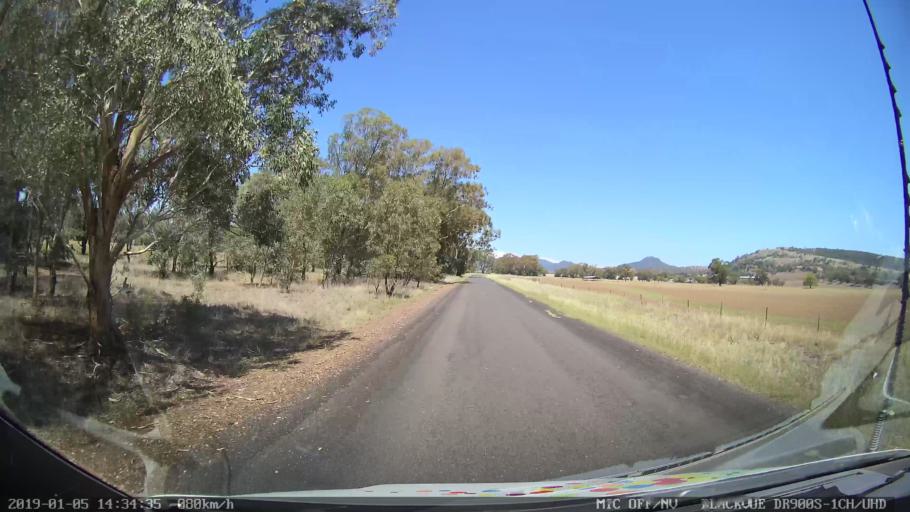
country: AU
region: New South Wales
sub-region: Tamworth Municipality
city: Phillip
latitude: -31.2340
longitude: 150.6432
